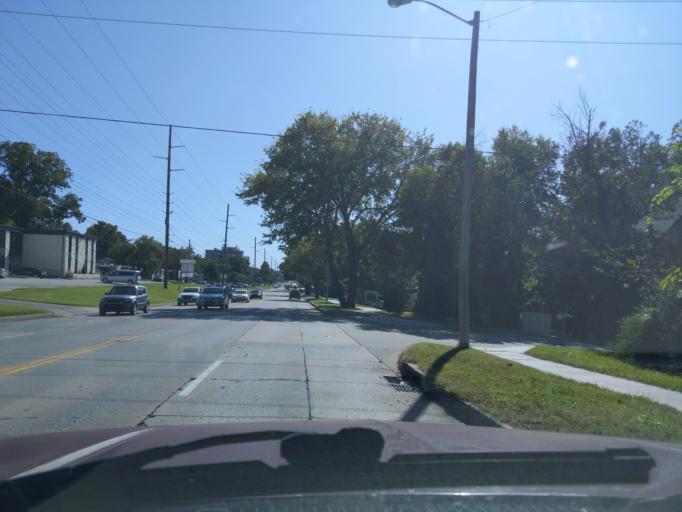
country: US
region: Oklahoma
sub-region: Tulsa County
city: Jenks
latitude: 36.0845
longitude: -95.9580
